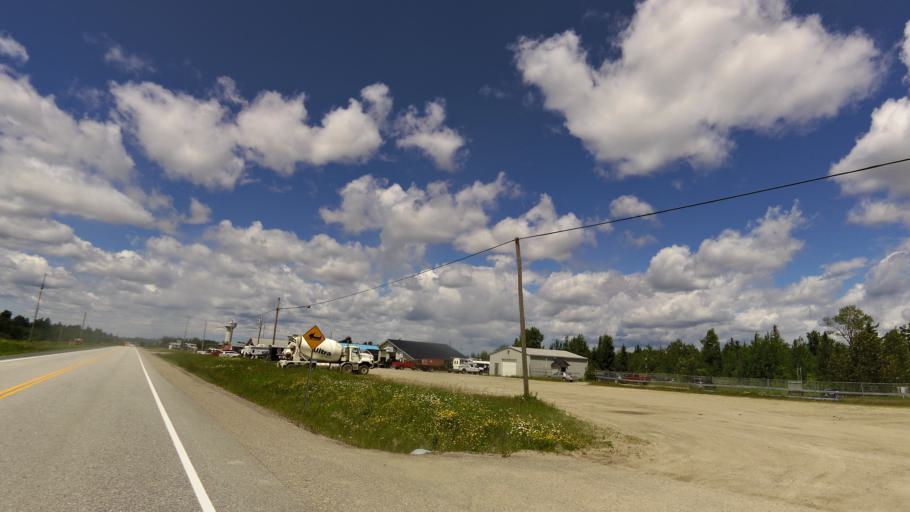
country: CA
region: Ontario
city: Kapuskasing
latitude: 49.2714
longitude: -81.6140
